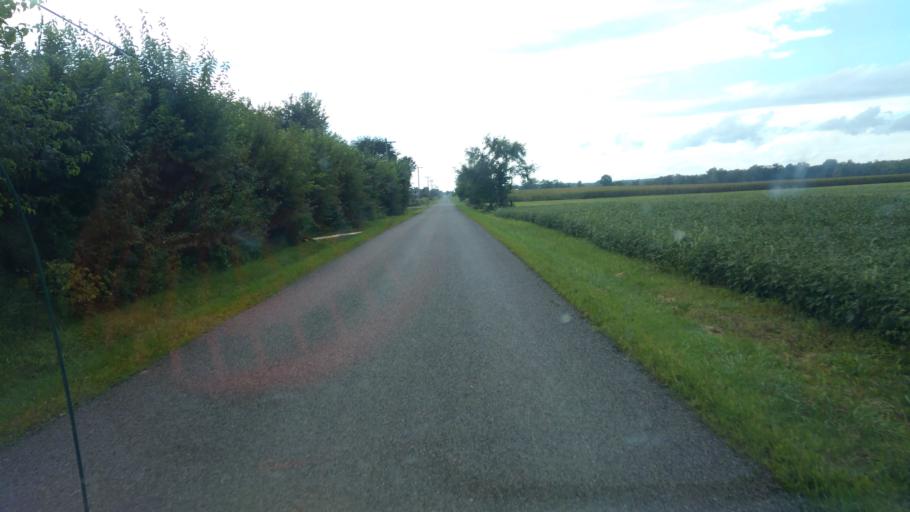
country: US
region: Ohio
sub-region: Hardin County
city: Kenton
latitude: 40.7037
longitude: -83.6216
